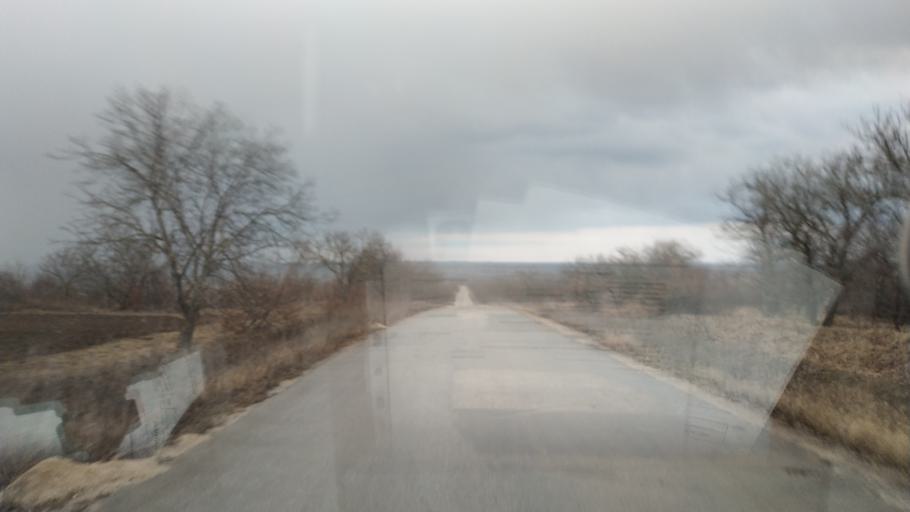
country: MD
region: Telenesti
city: Grigoriopol
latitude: 47.0706
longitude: 29.3057
